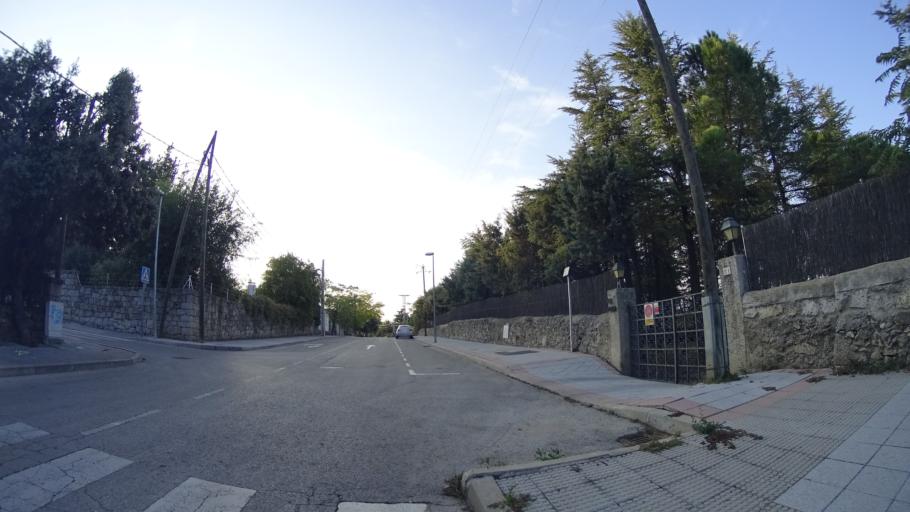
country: ES
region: Madrid
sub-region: Provincia de Madrid
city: Galapagar
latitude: 40.5760
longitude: -3.9925
